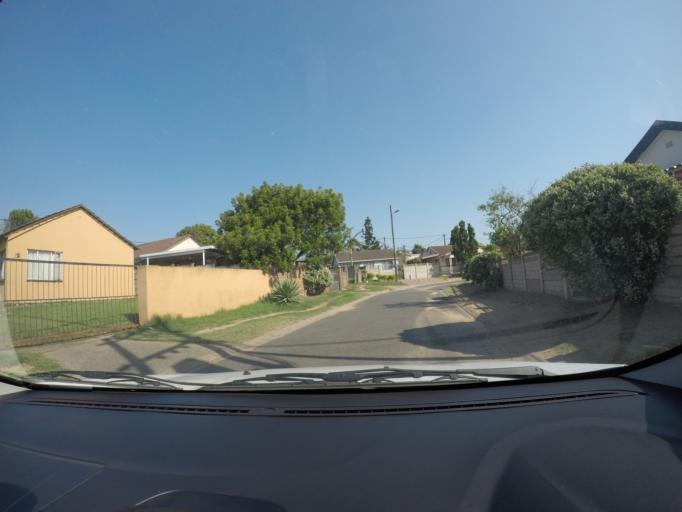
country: ZA
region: KwaZulu-Natal
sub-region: uThungulu District Municipality
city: Richards Bay
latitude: -28.7169
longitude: 32.0408
